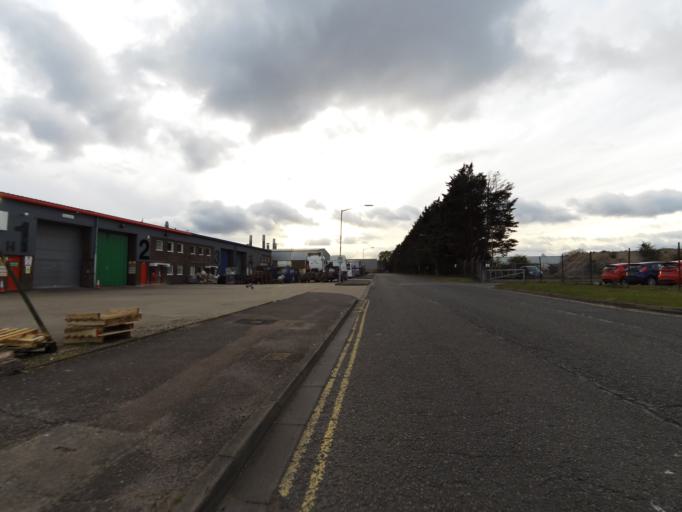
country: GB
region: England
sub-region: Suffolk
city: Kesgrave
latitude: 52.0299
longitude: 1.2073
